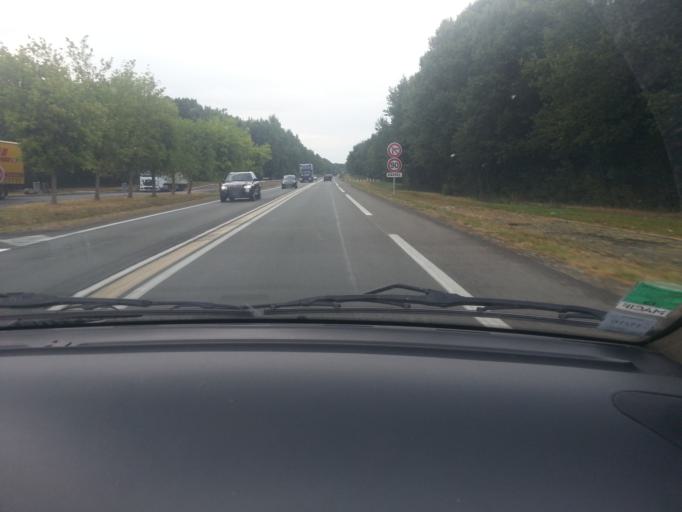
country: FR
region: Bourgogne
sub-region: Departement de Saone-et-Loire
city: Palinges
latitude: 46.5234
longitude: 4.1648
